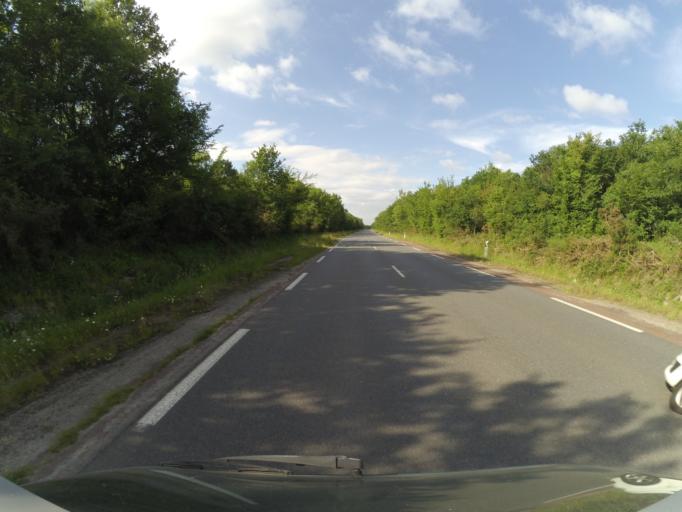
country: FR
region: Poitou-Charentes
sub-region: Departement de la Charente-Maritime
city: Saint-Agnant
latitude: 45.8022
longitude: -0.9357
